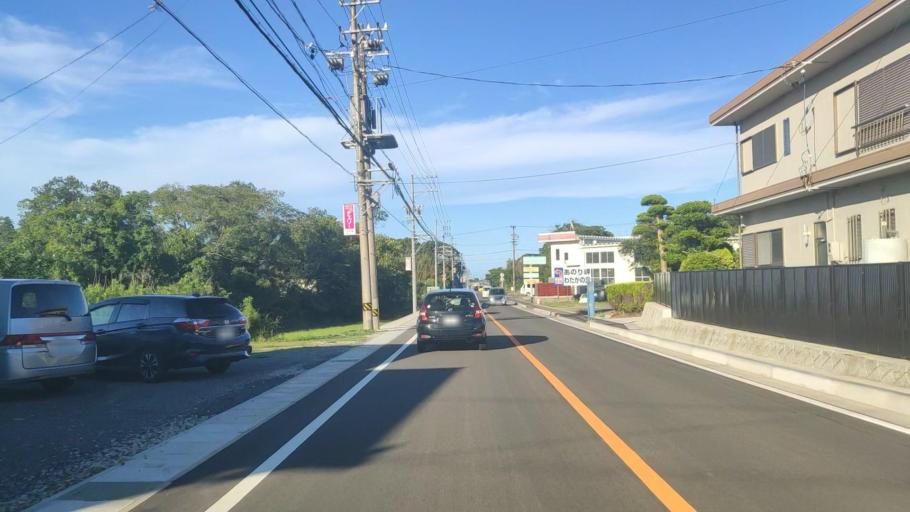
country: JP
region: Mie
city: Toba
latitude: 34.3348
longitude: 136.8685
